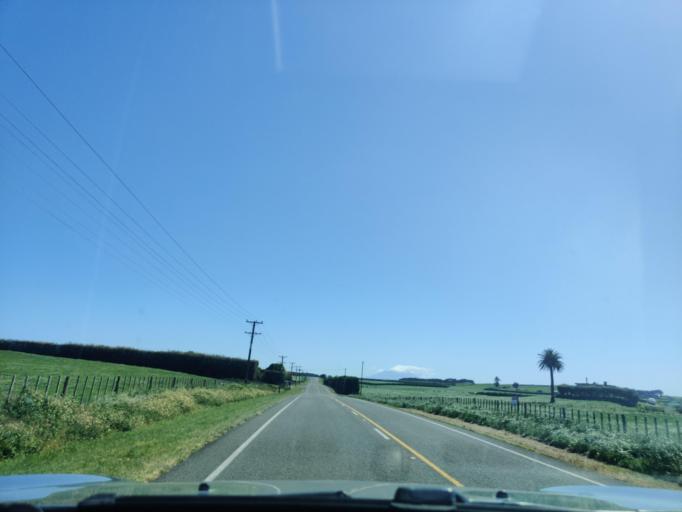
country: NZ
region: Taranaki
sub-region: South Taranaki District
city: Patea
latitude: -39.7019
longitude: 174.4378
